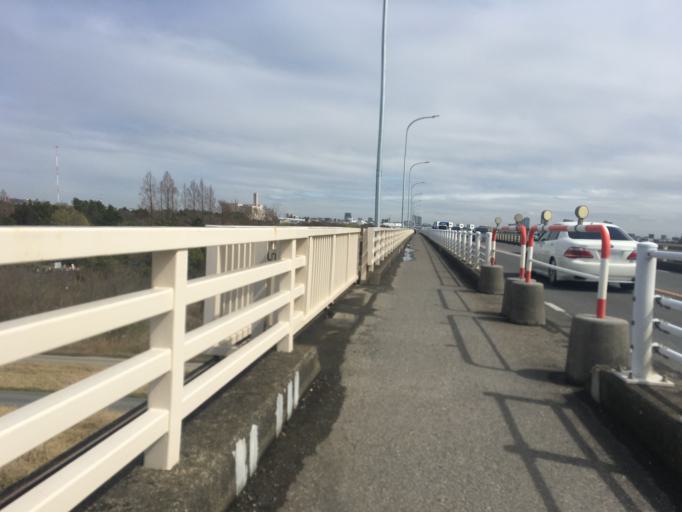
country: JP
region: Saitama
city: Shiki
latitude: 35.8370
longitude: 139.6093
